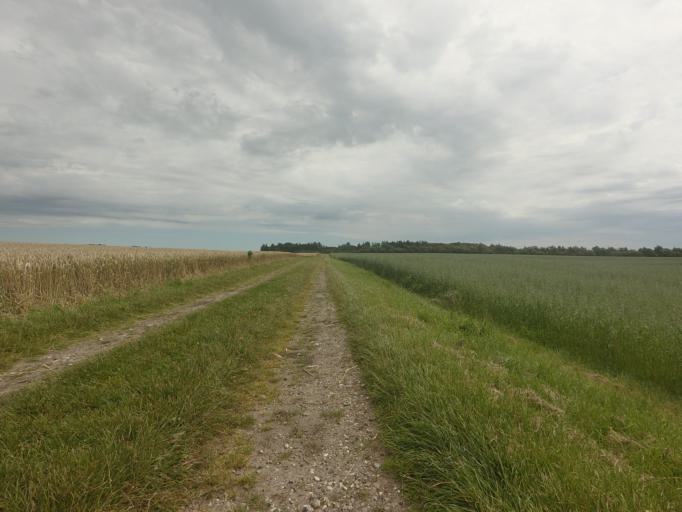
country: DK
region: North Denmark
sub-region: Hjorring Kommune
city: Vra
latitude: 57.3633
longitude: 9.7910
